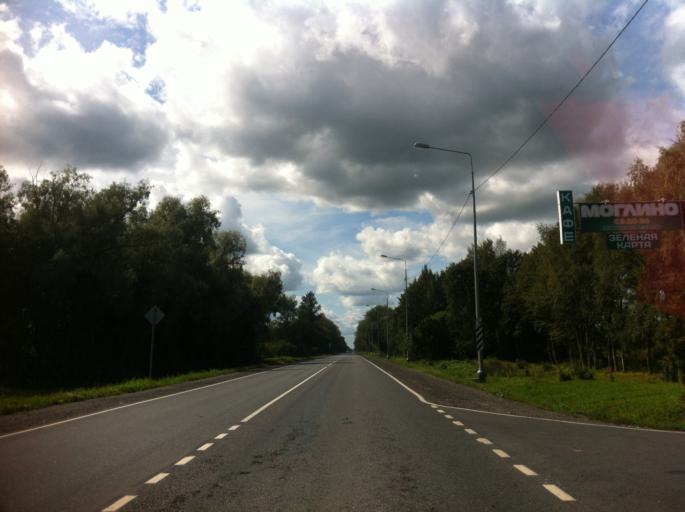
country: RU
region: Pskov
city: Pskov
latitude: 57.7794
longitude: 28.1608
